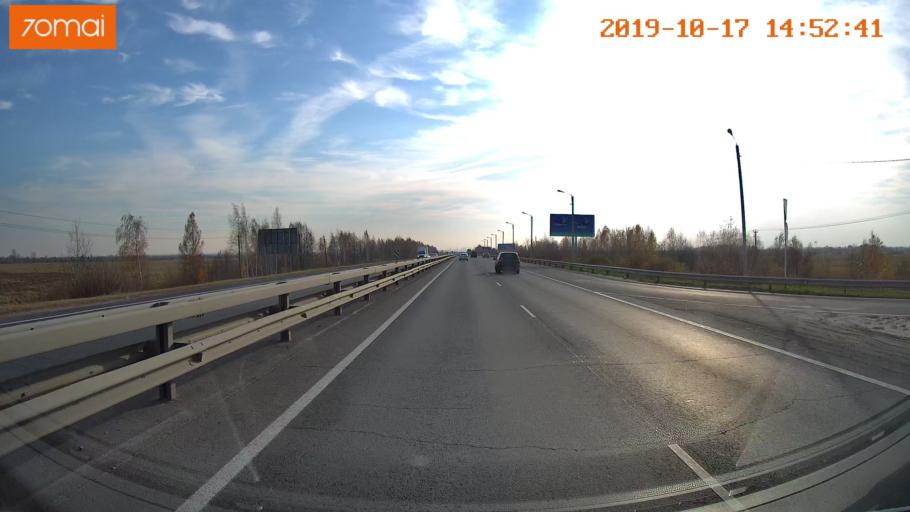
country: RU
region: Rjazan
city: Polyany
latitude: 54.7044
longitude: 39.8440
